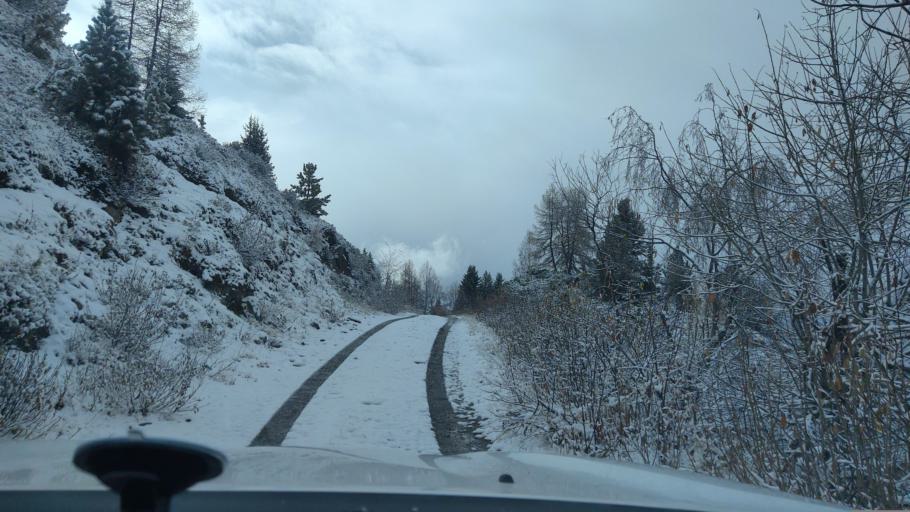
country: FR
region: Rhone-Alpes
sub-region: Departement de la Savoie
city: Seez
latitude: 45.5845
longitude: 6.8020
